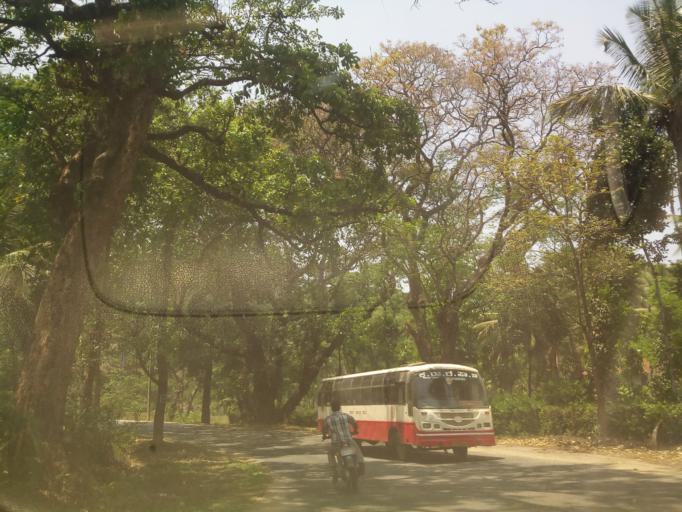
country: IN
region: Karnataka
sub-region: Hassan
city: Sakleshpur
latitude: 12.9549
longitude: 75.8353
